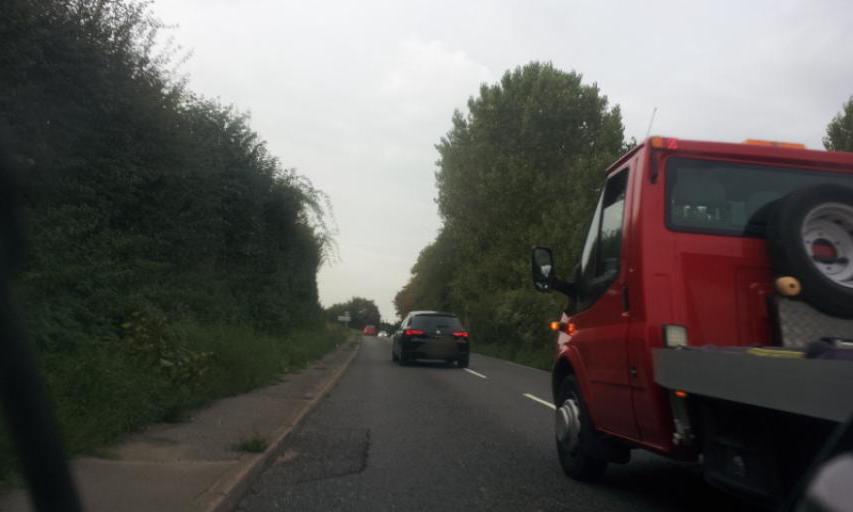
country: GB
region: England
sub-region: Kent
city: Wateringbury
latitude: 51.2404
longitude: 0.4107
